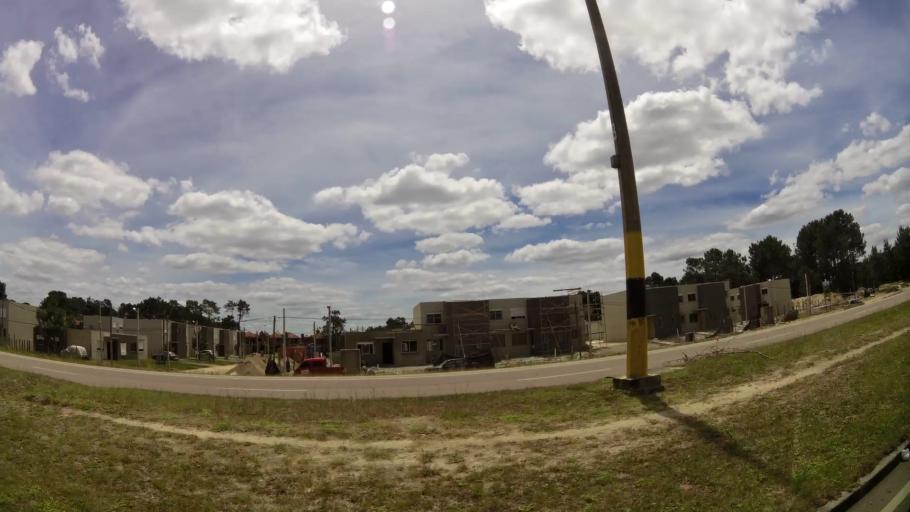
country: UY
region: Canelones
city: Pando
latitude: -34.7983
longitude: -55.9158
